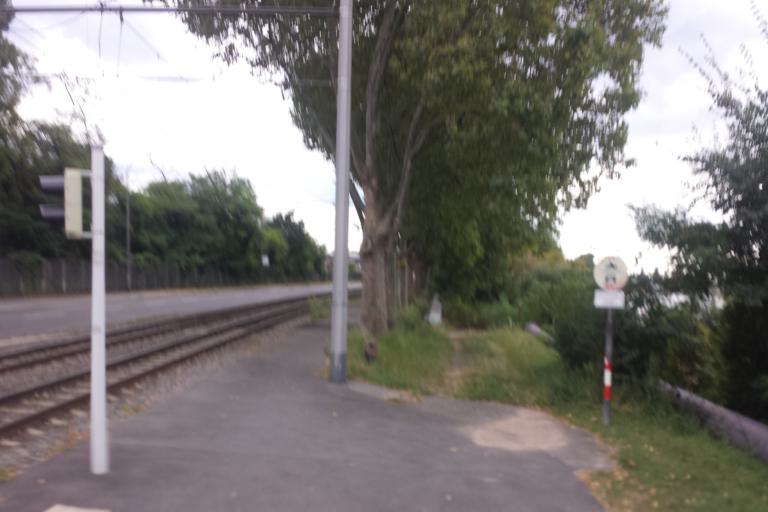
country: DE
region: Baden-Wuerttemberg
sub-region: Karlsruhe Region
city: Mannheim
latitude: 49.5252
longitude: 8.4712
